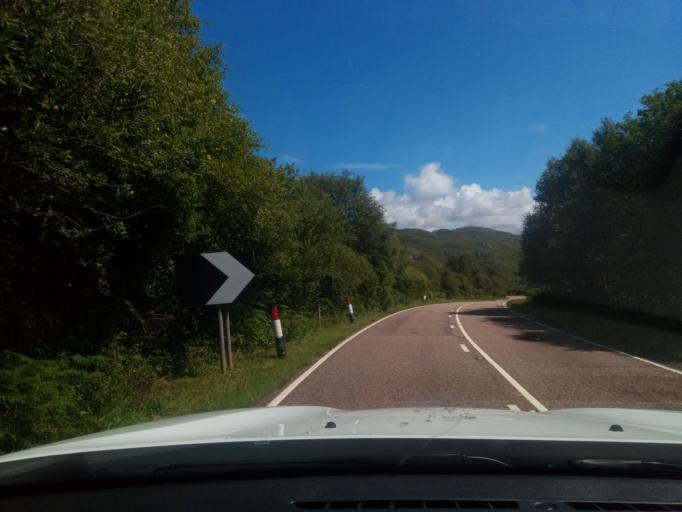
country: GB
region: Scotland
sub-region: Argyll and Bute
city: Isle Of Mull
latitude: 56.8857
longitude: -5.6493
